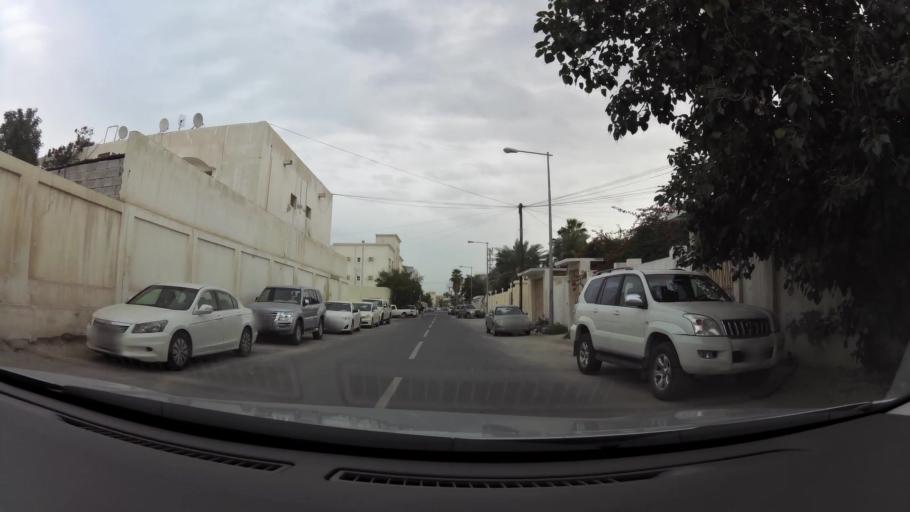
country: QA
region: Baladiyat ad Dawhah
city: Doha
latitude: 25.3175
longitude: 51.4926
